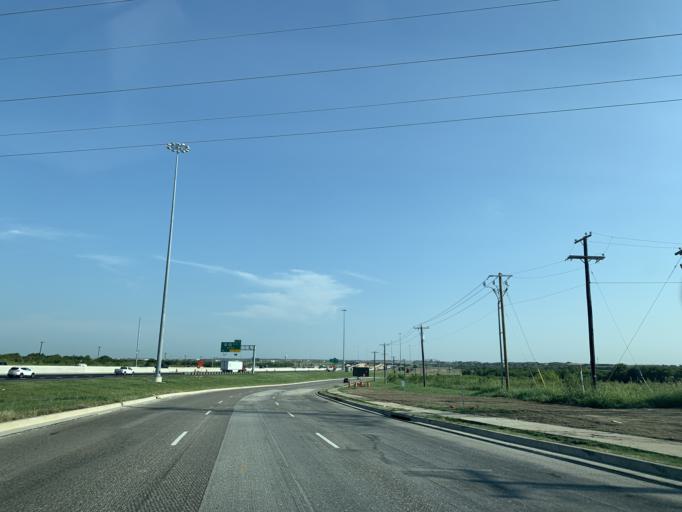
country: US
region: Texas
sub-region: Tarrant County
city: Blue Mound
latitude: 32.8754
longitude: -97.3163
